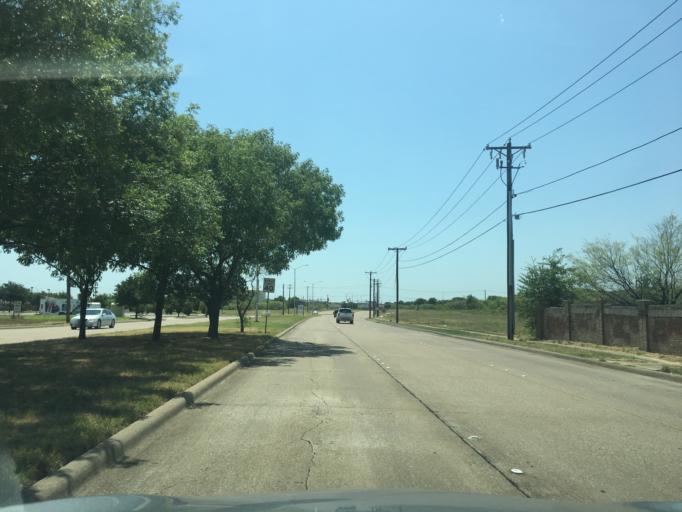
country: US
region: Texas
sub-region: Tarrant County
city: Crowley
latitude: 32.6174
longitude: -97.3707
